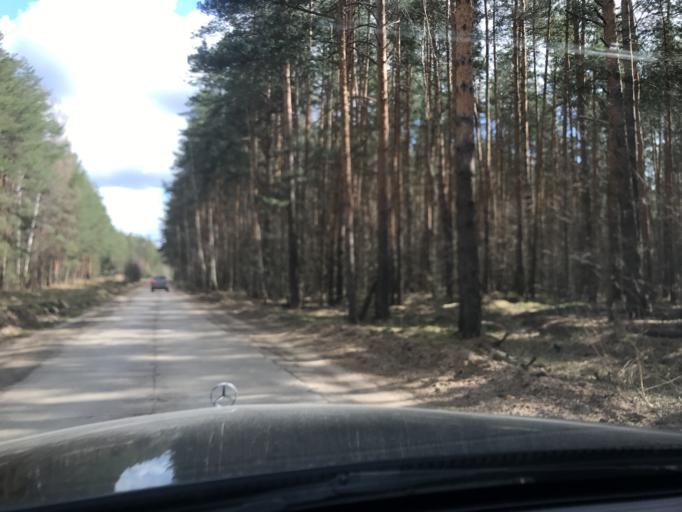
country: RU
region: Moskovskaya
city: Vereya
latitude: 55.8383
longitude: 39.0870
